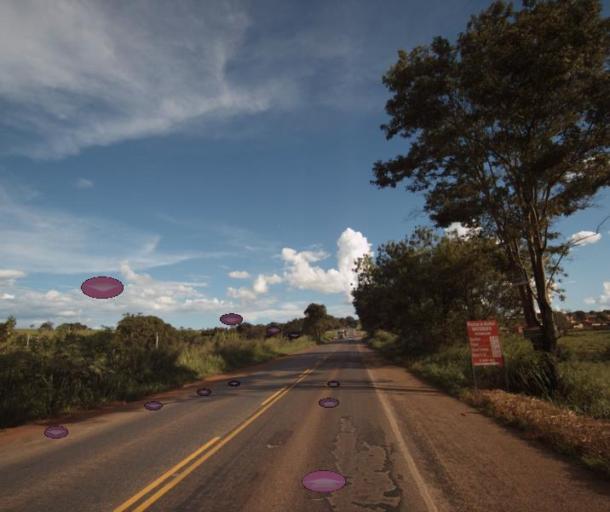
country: BR
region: Goias
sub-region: Rialma
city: Rialma
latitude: -15.3074
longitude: -49.5715
